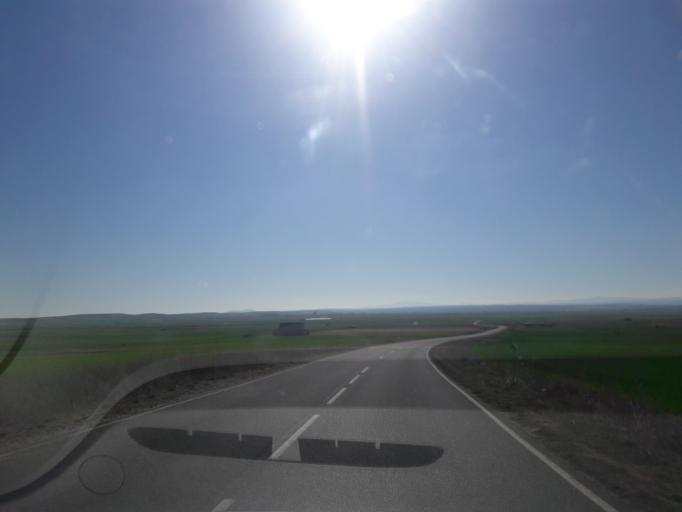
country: ES
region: Castille and Leon
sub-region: Provincia de Salamanca
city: Santiago de la Puebla
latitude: 40.8189
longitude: -5.2635
